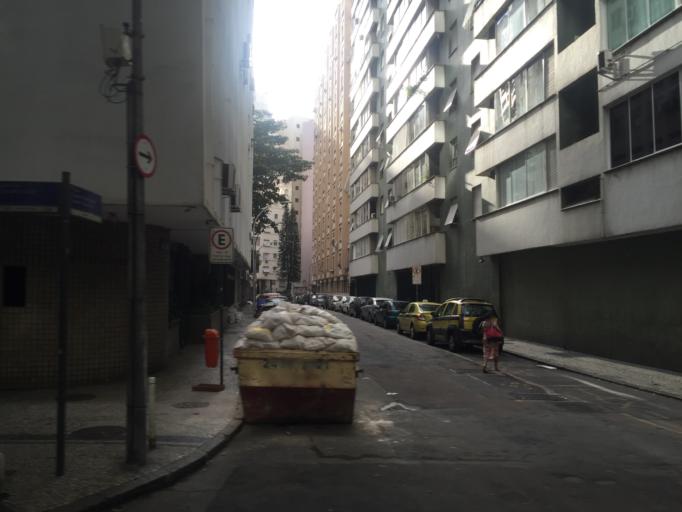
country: BR
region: Rio de Janeiro
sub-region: Rio De Janeiro
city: Rio de Janeiro
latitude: -22.9405
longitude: -43.1759
